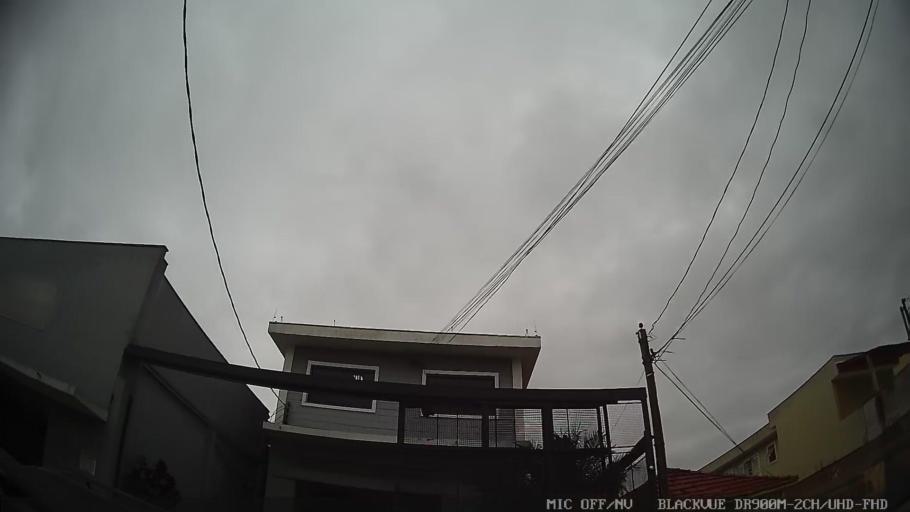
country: BR
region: Sao Paulo
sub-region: Osasco
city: Osasco
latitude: -23.5125
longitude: -46.7431
